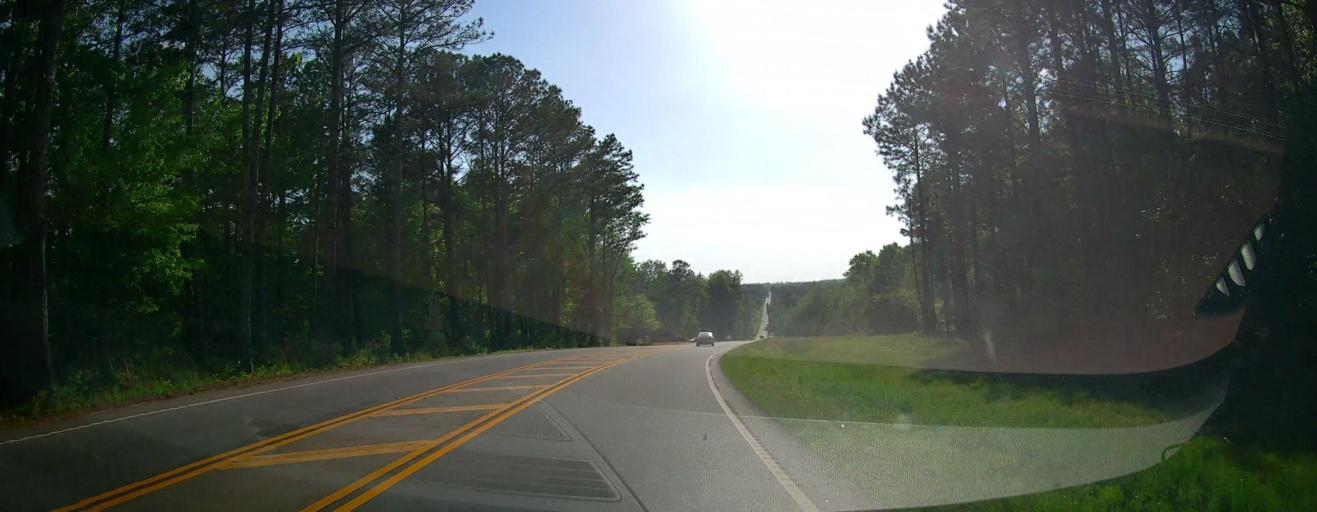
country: US
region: Georgia
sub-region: Walton County
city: Social Circle
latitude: 33.6082
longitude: -83.7014
